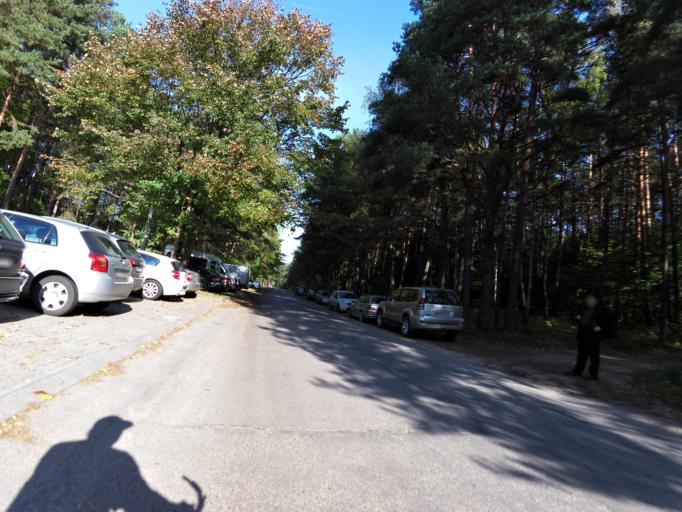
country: LT
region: Vilnius County
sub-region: Vilnius
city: Vilnius
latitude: 54.7363
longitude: 25.2945
